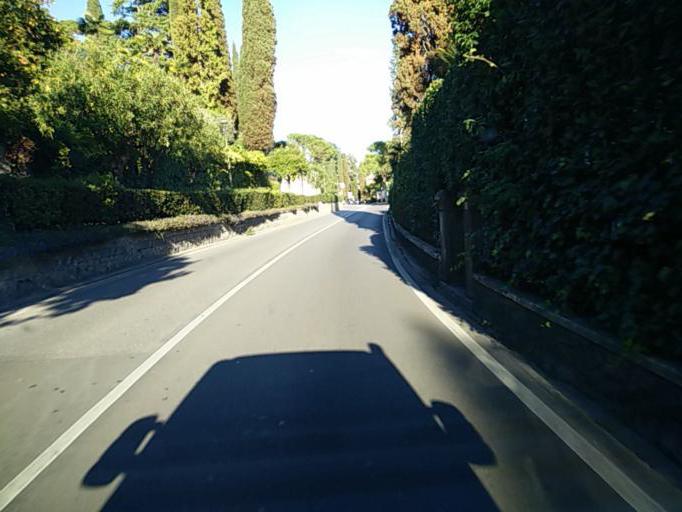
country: IT
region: Lombardy
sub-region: Provincia di Brescia
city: Gardone Riviera
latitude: 45.6218
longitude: 10.5684
